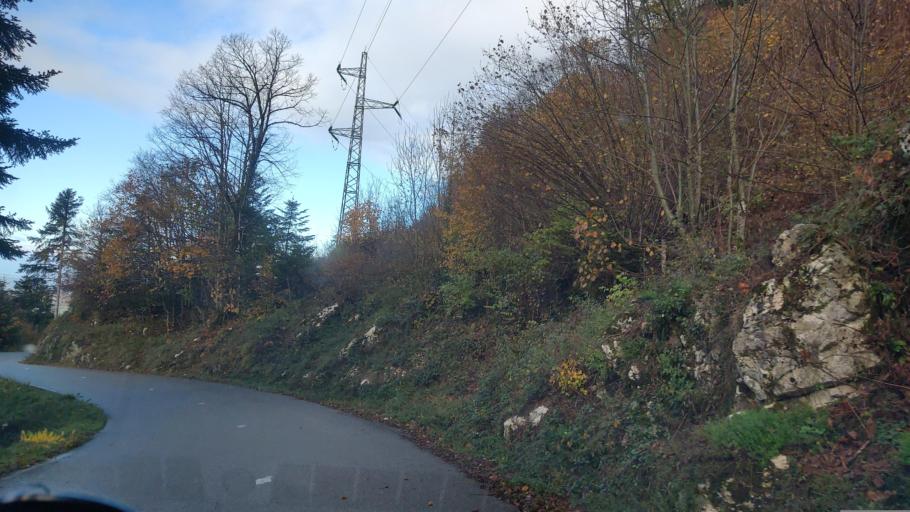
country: FR
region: Rhone-Alpes
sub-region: Departement de la Savoie
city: Novalaise
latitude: 45.5882
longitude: 5.8084
